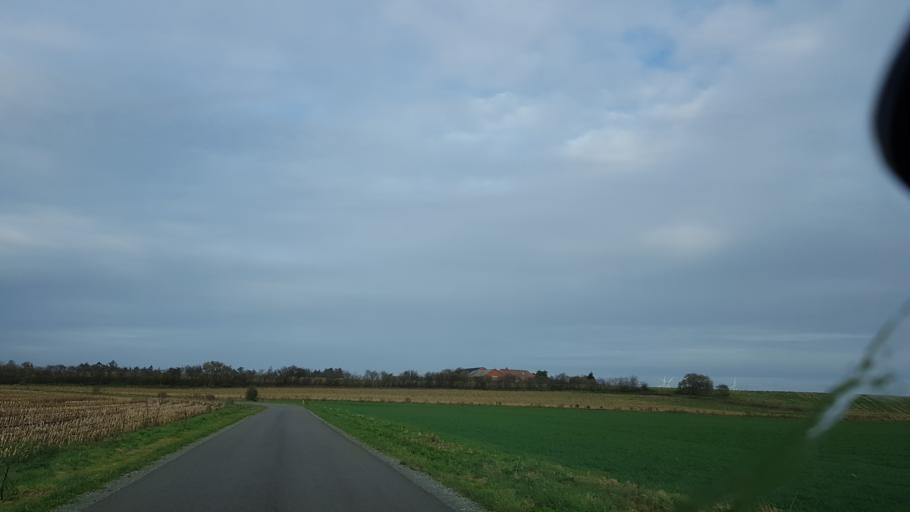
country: DK
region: South Denmark
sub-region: Haderslev Kommune
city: Gram
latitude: 55.2548
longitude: 9.0691
